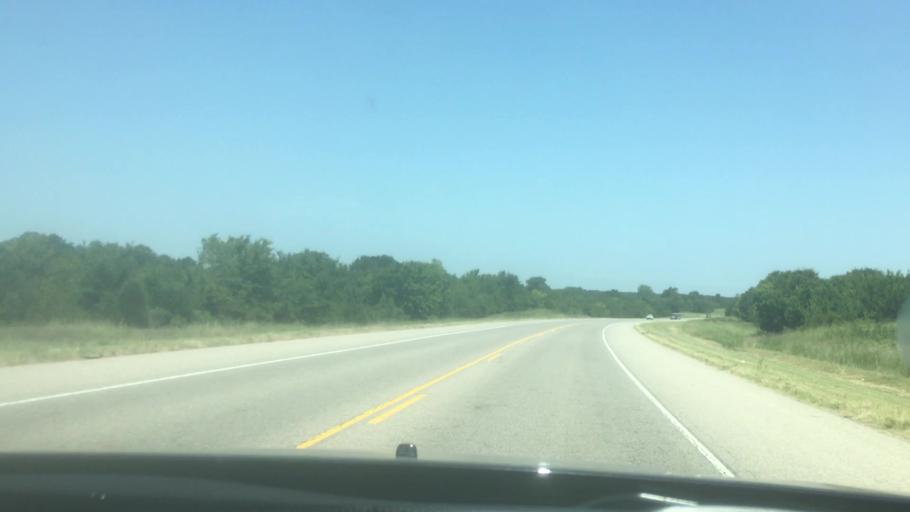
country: US
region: Oklahoma
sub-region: Pontotoc County
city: Ada
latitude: 34.6462
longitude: -96.5494
